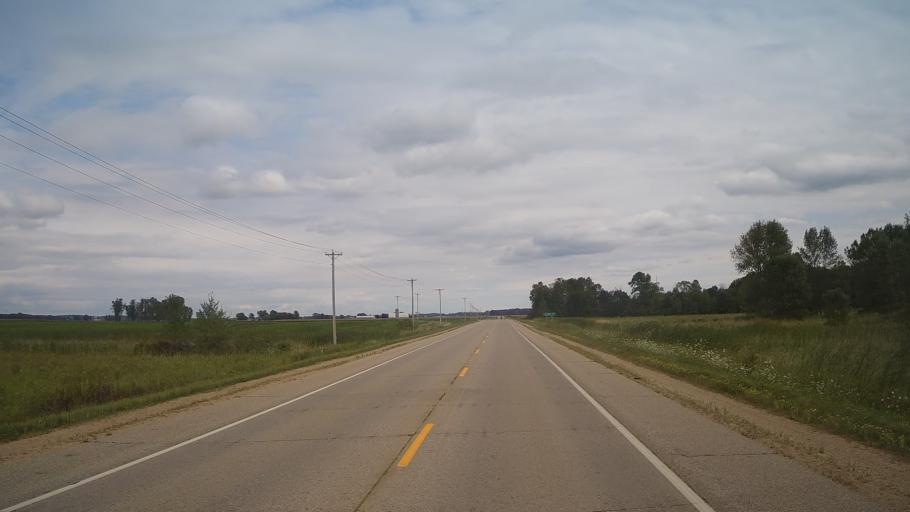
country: US
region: Wisconsin
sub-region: Waushara County
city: Redgranite
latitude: 44.0375
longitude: -89.0669
